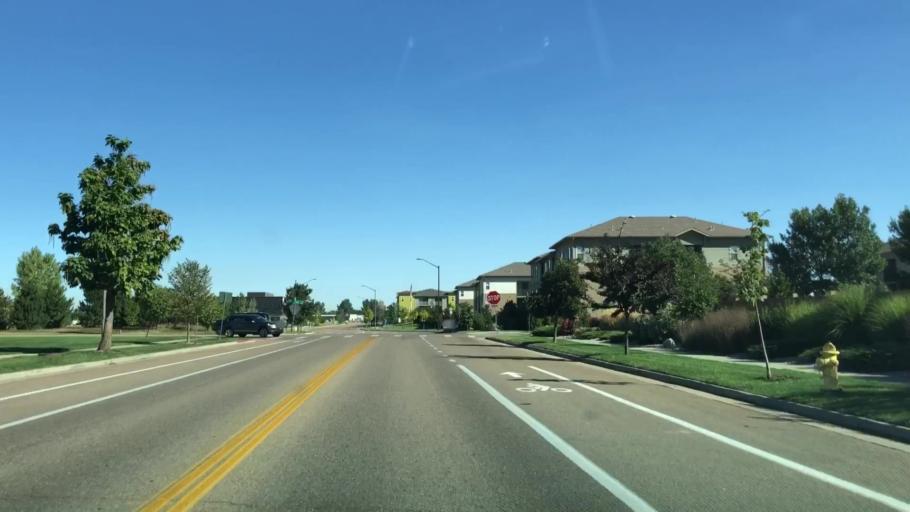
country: US
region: Colorado
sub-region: Larimer County
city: Fort Collins
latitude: 40.5154
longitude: -105.0105
